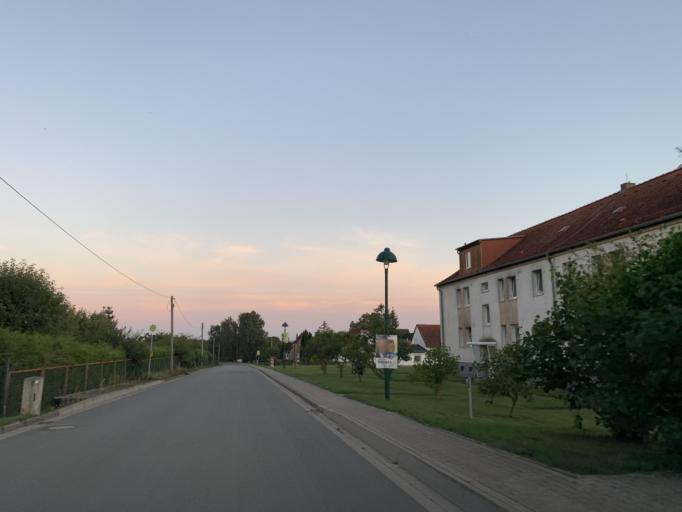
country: DE
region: Mecklenburg-Vorpommern
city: Blankensee
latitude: 53.4426
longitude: 13.2996
